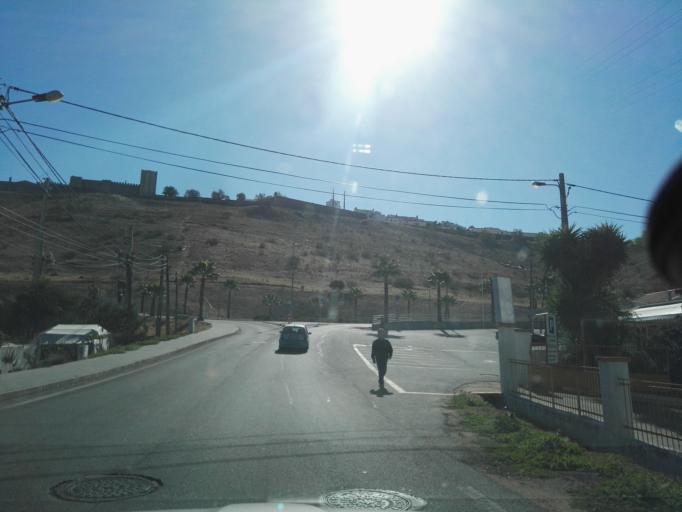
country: PT
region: Portalegre
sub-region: Elvas
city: Elvas
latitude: 38.8856
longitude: -7.1667
